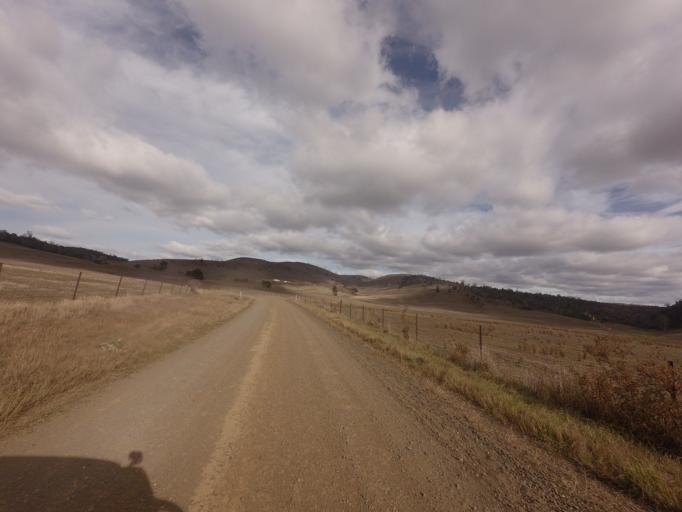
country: AU
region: Tasmania
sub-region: Brighton
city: Bridgewater
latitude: -42.4642
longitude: 147.2777
